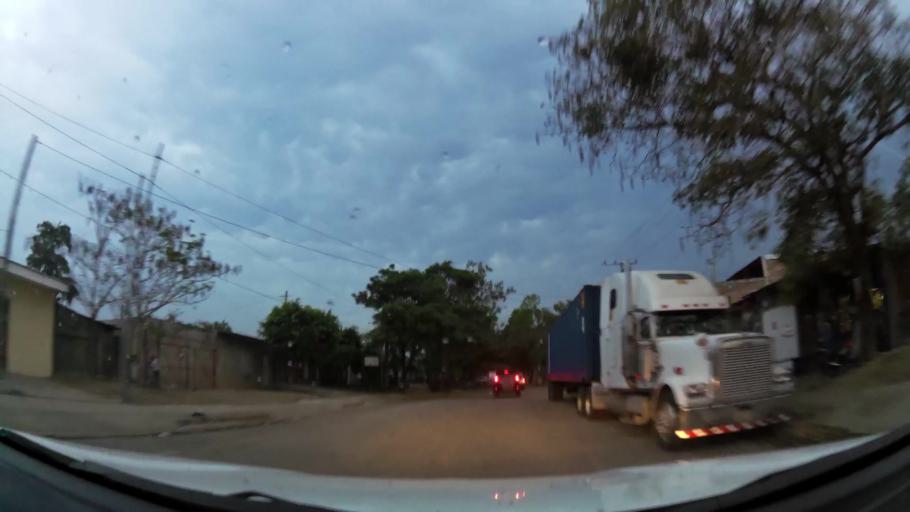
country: NI
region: Esteli
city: Esteli
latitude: 13.1050
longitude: -86.3586
